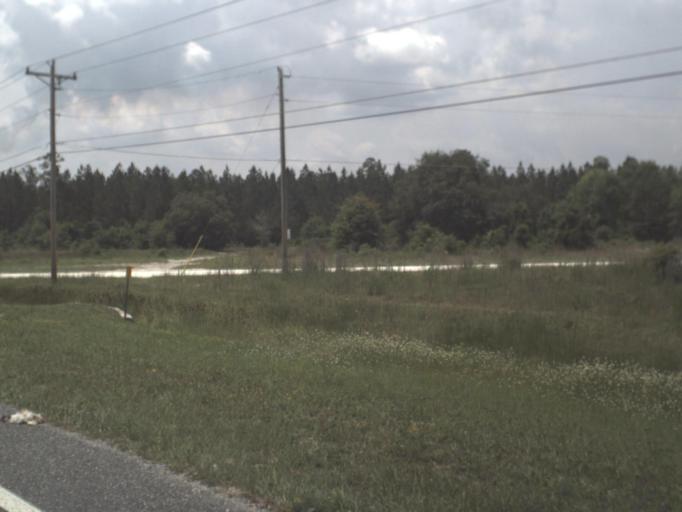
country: US
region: Florida
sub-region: Putnam County
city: East Palatka
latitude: 29.7825
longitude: -81.6443
